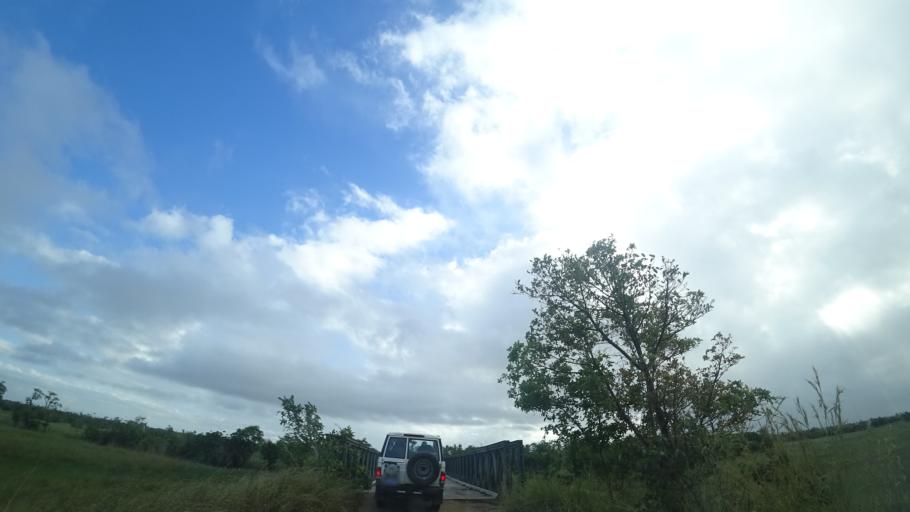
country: MZ
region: Sofala
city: Beira
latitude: -19.6305
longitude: 35.0600
